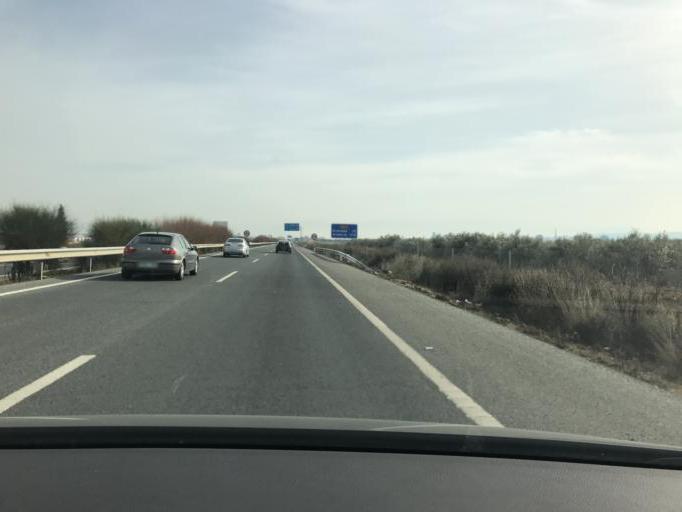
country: ES
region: Andalusia
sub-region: Provincia de Granada
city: Cijuela
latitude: 37.1933
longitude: -3.7958
